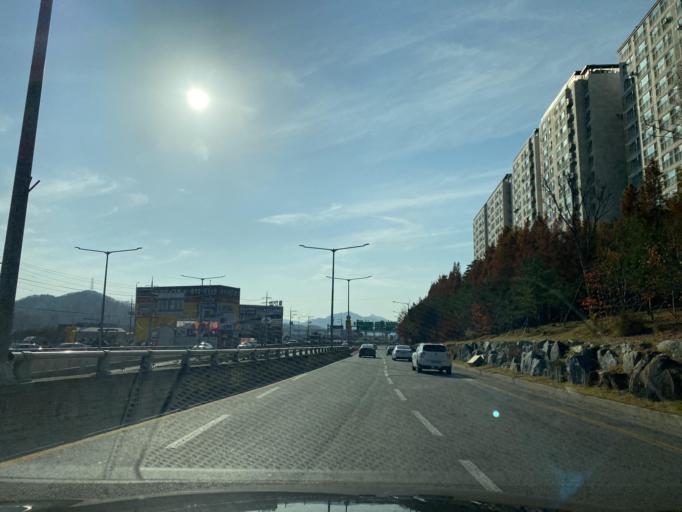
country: KR
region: Chungcheongnam-do
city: Cheonan
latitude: 36.7860
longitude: 127.1169
